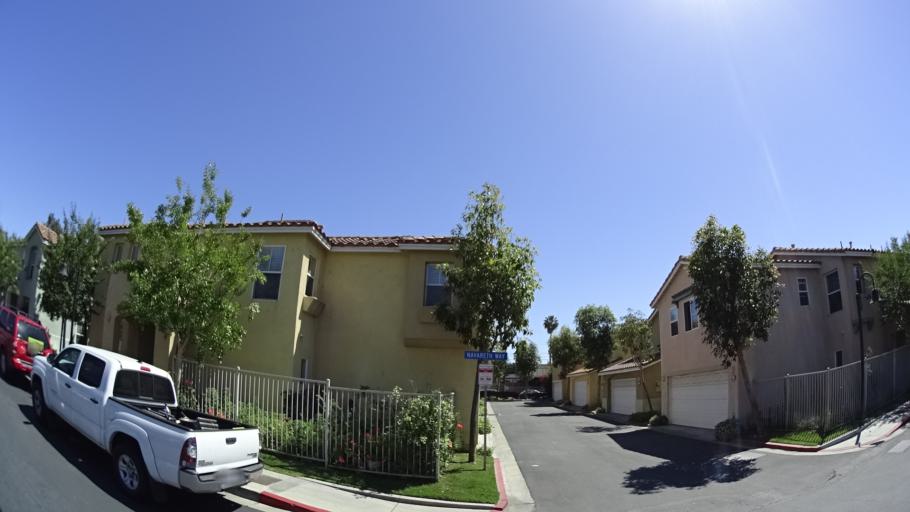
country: US
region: California
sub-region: Los Angeles County
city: Los Angeles
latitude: 34.0485
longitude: -118.2231
